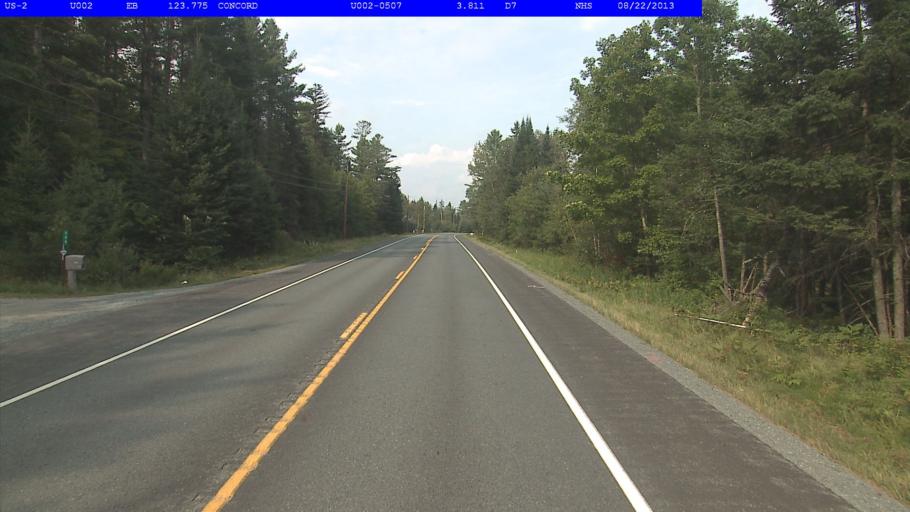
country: US
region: Vermont
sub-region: Caledonia County
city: St Johnsbury
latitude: 44.4485
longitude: -71.8738
